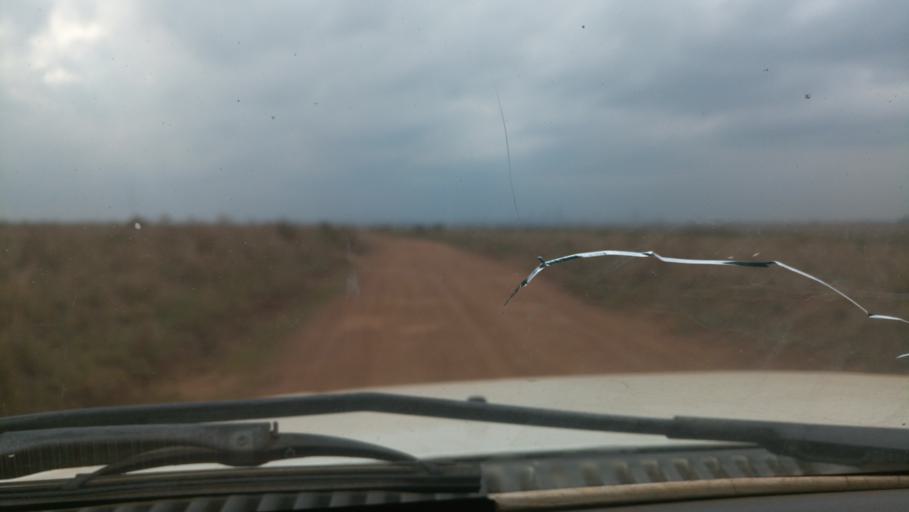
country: KE
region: Nairobi Area
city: Nairobi
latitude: -1.3607
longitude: 36.8282
